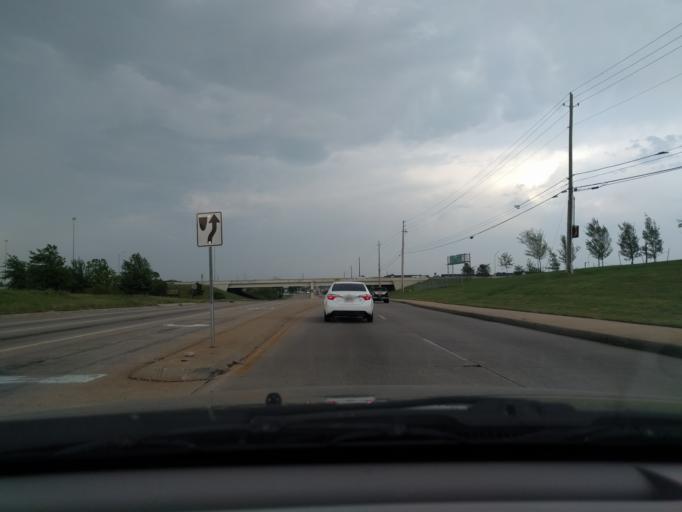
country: US
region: Oklahoma
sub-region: Tulsa County
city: Broken Arrow
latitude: 36.0464
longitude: -95.8616
